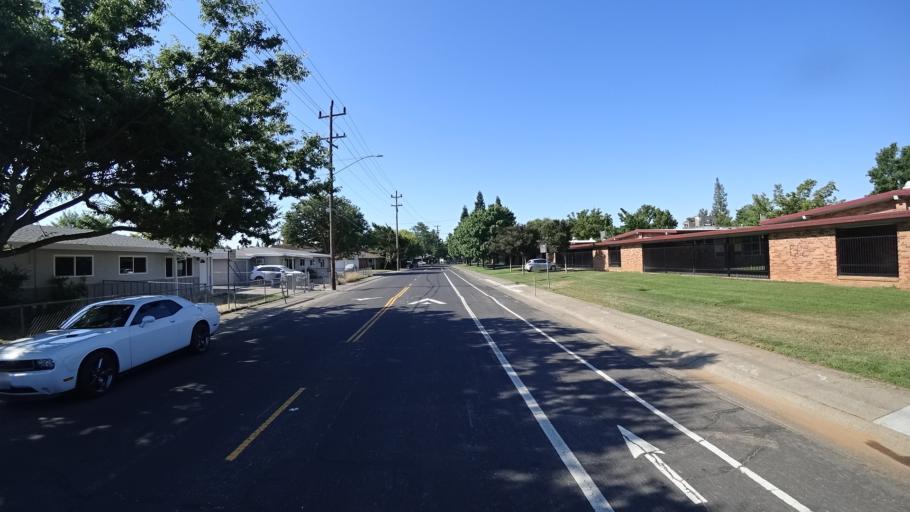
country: US
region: California
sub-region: Sacramento County
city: Florin
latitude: 38.5409
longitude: -121.4232
